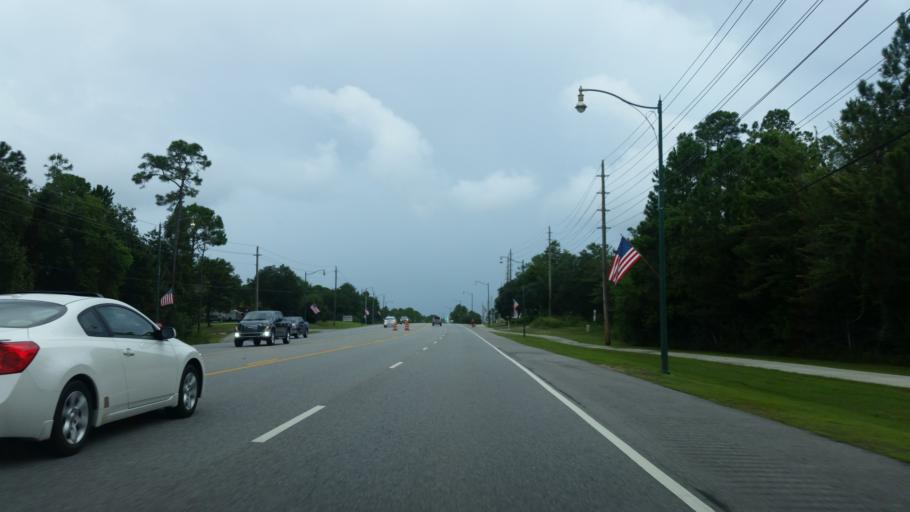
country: US
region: Alabama
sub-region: Baldwin County
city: Orange Beach
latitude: 30.2880
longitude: -87.5814
